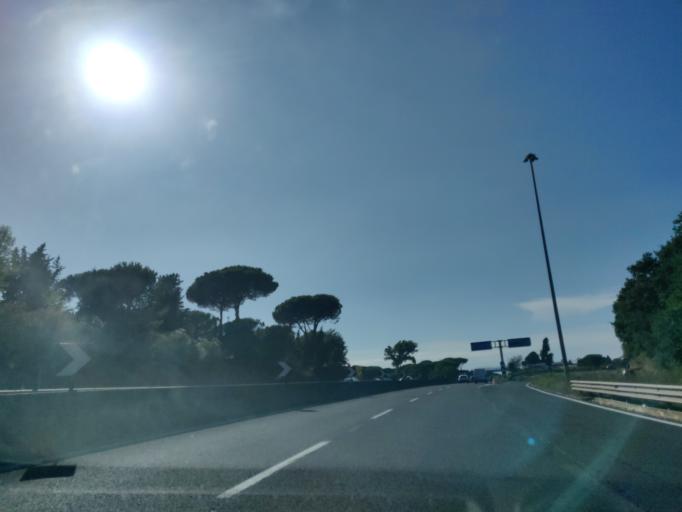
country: IT
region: Latium
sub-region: Citta metropolitana di Roma Capitale
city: Ara Nova
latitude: 41.9116
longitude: 12.2514
